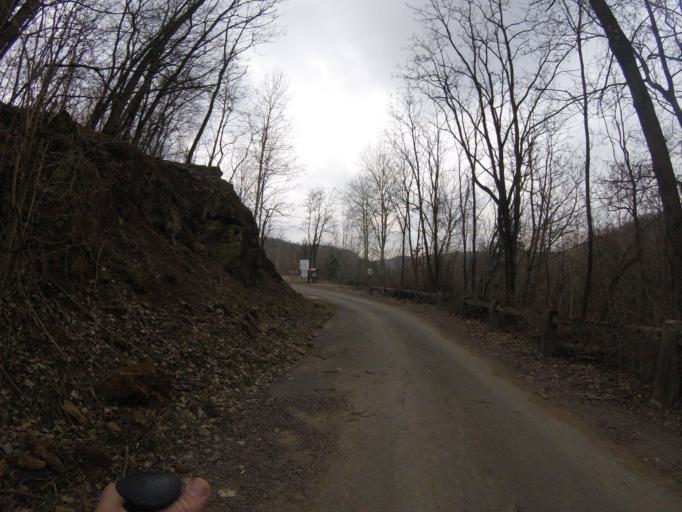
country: HU
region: Borsod-Abauj-Zemplen
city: Rudabanya
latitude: 48.3958
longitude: 20.6457
